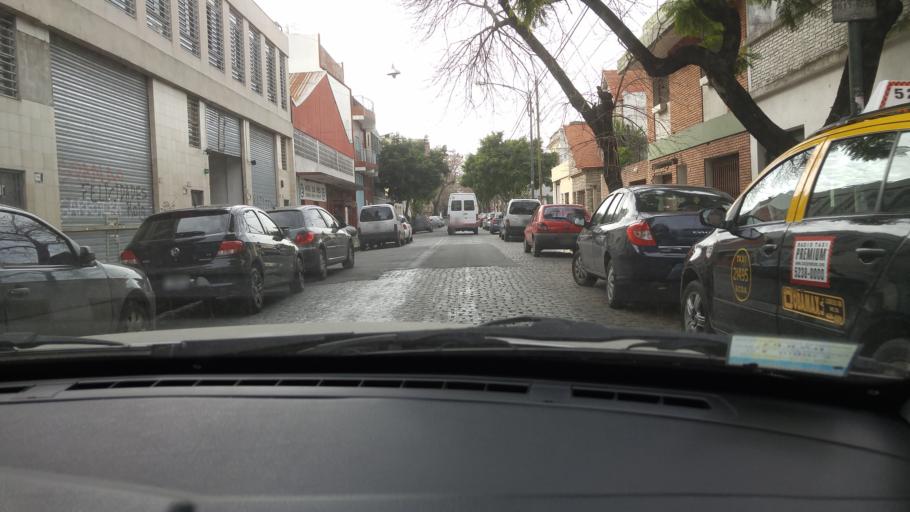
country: AR
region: Buenos Aires F.D.
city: Villa Santa Rita
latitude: -34.6275
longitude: -58.4859
